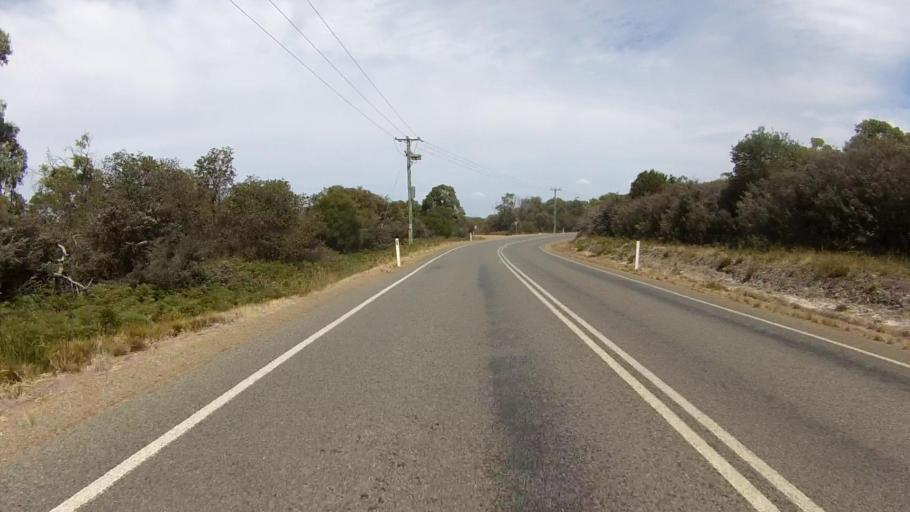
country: AU
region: Tasmania
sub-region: Clarence
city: Sandford
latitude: -43.0228
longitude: 147.4874
